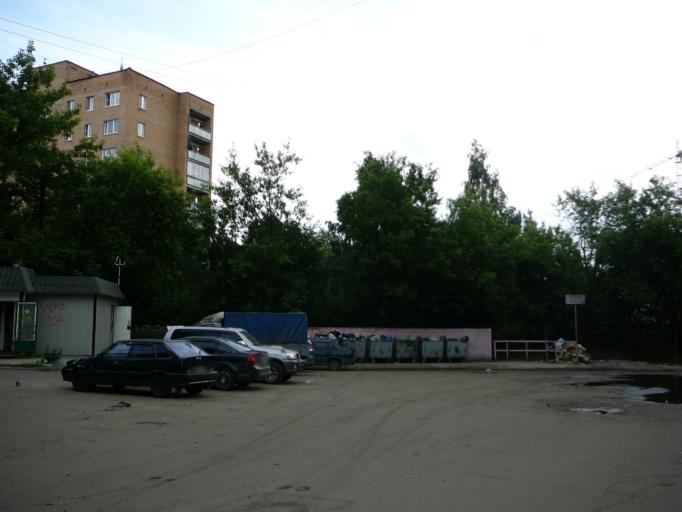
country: RU
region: Moskovskaya
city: Krasnogorsk
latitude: 55.8165
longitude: 37.3378
